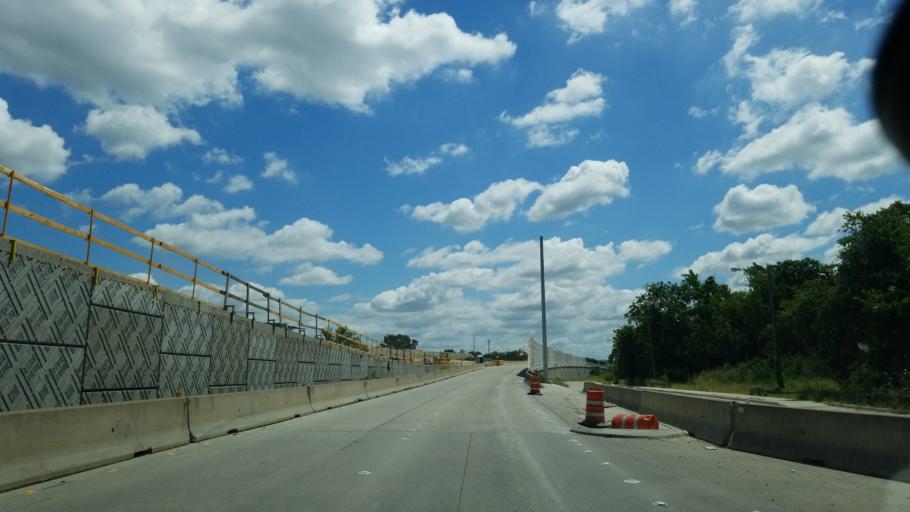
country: US
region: Texas
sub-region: Dallas County
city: Dallas
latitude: 32.7462
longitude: -96.7566
